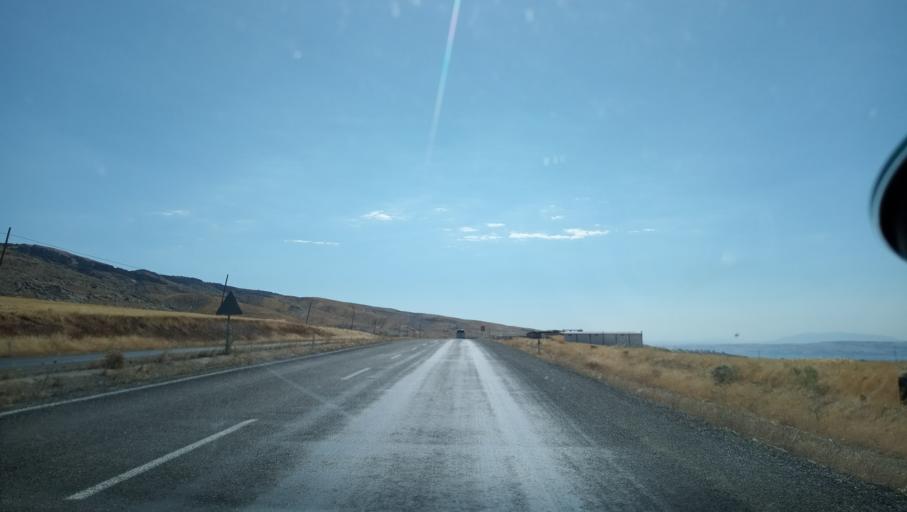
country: TR
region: Diyarbakir
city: Silvan
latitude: 38.1279
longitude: 41.0690
